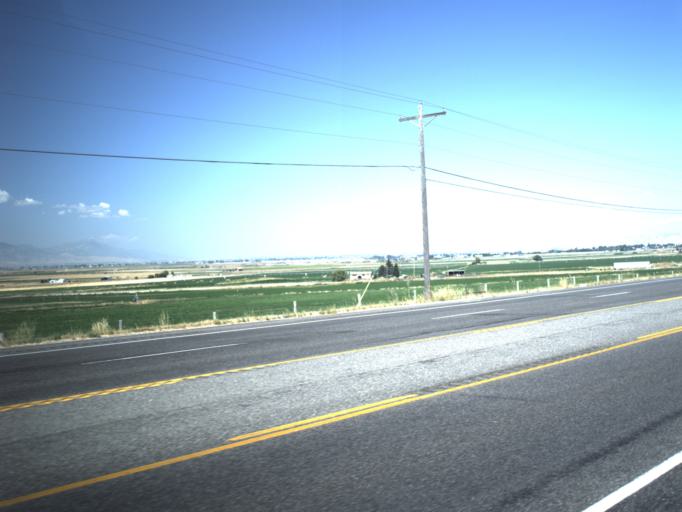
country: US
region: Utah
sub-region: Cache County
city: Smithfield
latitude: 41.8749
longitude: -111.8247
